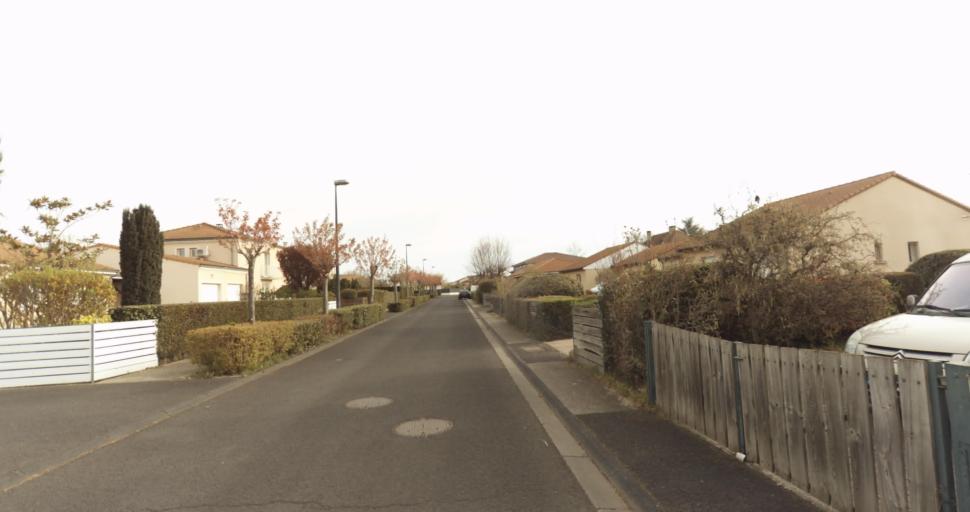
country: FR
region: Auvergne
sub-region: Departement du Puy-de-Dome
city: Cebazat
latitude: 45.8306
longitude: 3.1088
